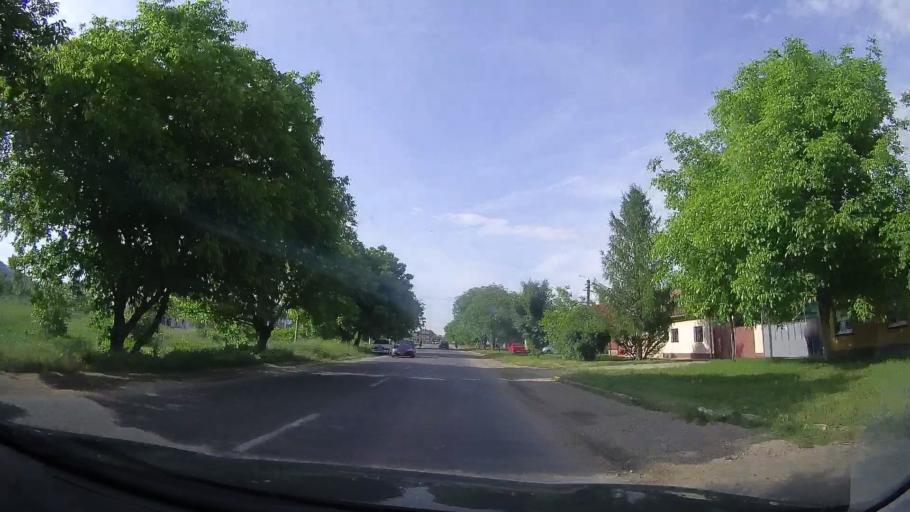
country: RO
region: Caras-Severin
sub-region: Municipiul Caransebes
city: Caransebes
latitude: 45.3906
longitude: 22.2280
